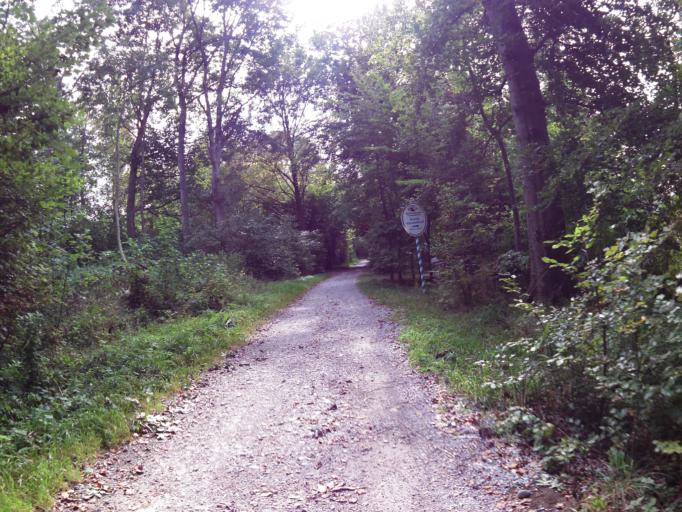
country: DE
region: Bavaria
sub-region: Upper Bavaria
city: Seeshaupt
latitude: 47.8271
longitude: 11.3378
